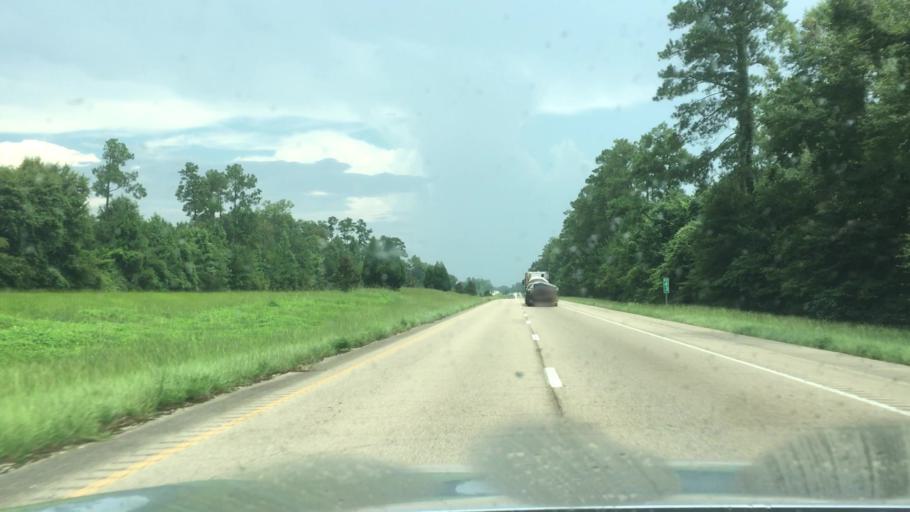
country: US
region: Mississippi
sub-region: Lamar County
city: Lumberton
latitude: 31.0206
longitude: -89.4085
